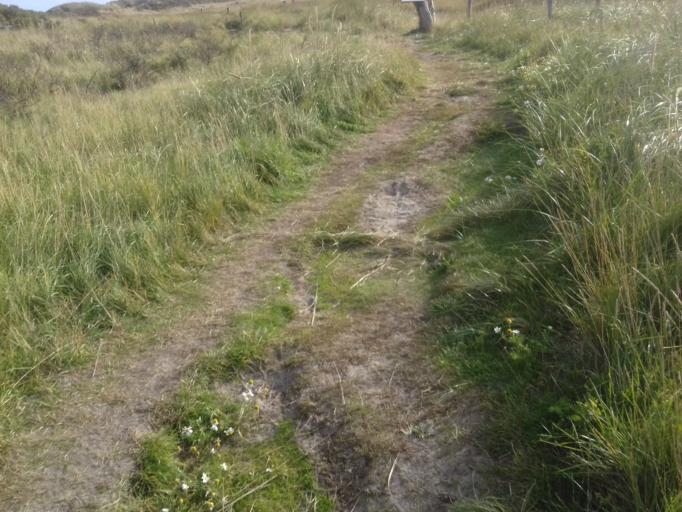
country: DE
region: Lower Saxony
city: Juist
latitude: 53.6802
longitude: 7.0641
